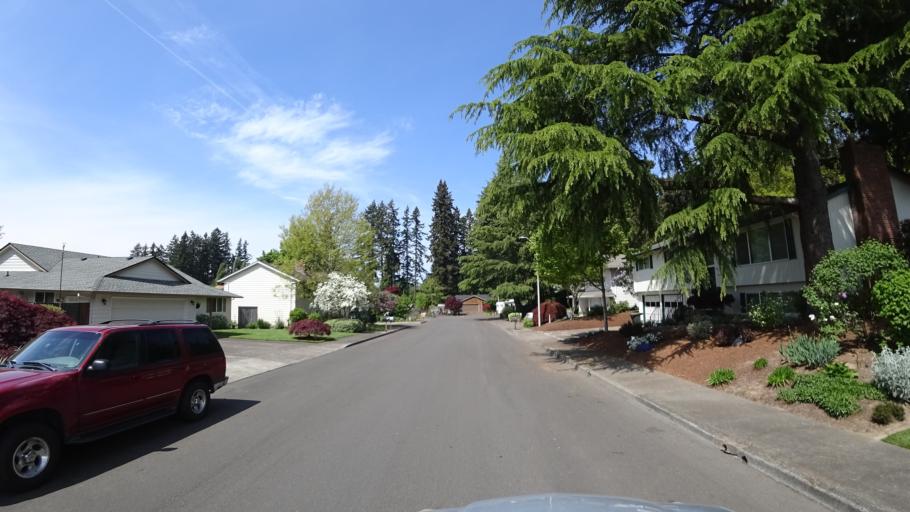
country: US
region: Oregon
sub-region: Washington County
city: Hillsboro
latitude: 45.5089
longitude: -122.9297
